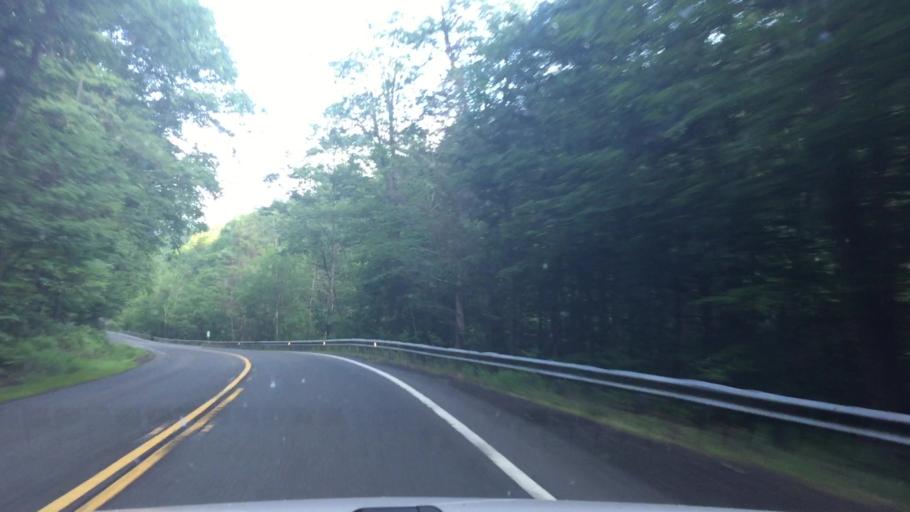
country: US
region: Massachusetts
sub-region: Hampshire County
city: Chesterfield
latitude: 42.3270
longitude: -72.8729
